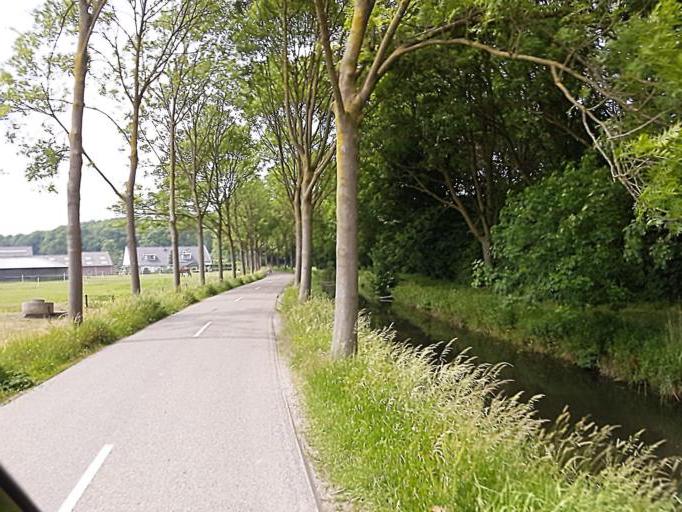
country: NL
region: Utrecht
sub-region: Gemeente Utrecht
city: Lunetten
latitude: 52.0532
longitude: 5.1500
